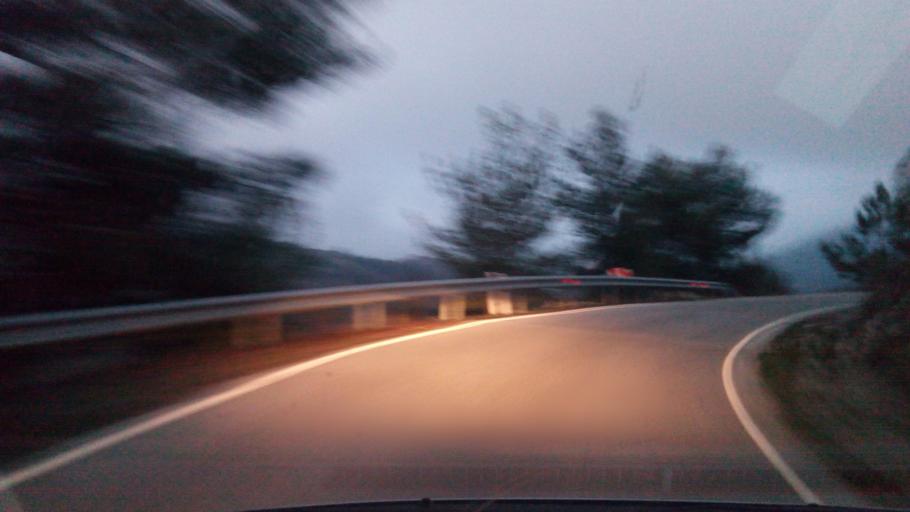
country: CY
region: Limassol
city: Kyperounta
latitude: 34.9057
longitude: 33.0885
